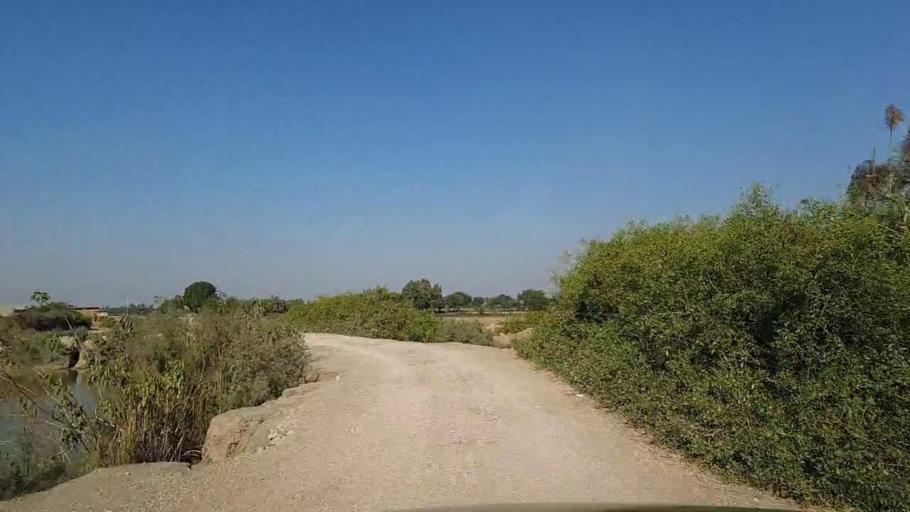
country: PK
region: Sindh
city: Mirpur Batoro
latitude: 24.7442
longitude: 68.3413
